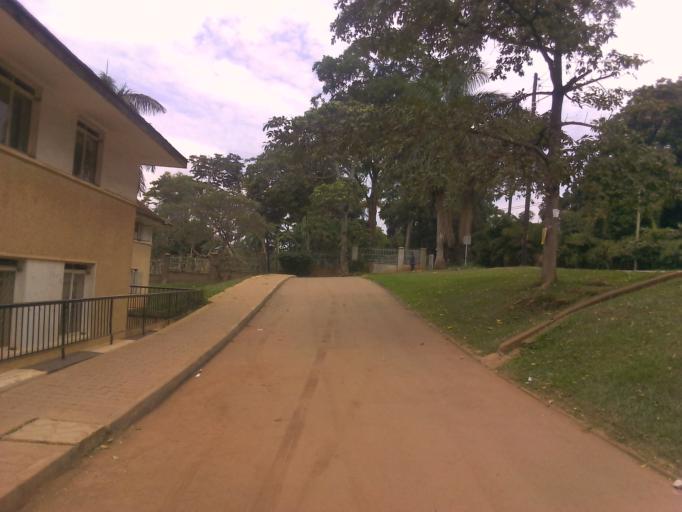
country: UG
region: Central Region
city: Kampala Central Division
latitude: 0.3380
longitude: 32.5688
